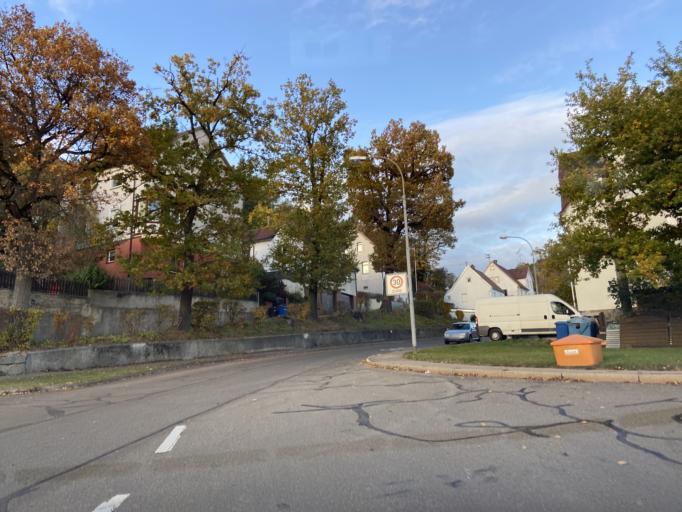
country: DE
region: Baden-Wuerttemberg
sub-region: Tuebingen Region
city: Sigmaringen
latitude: 48.0924
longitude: 9.2158
